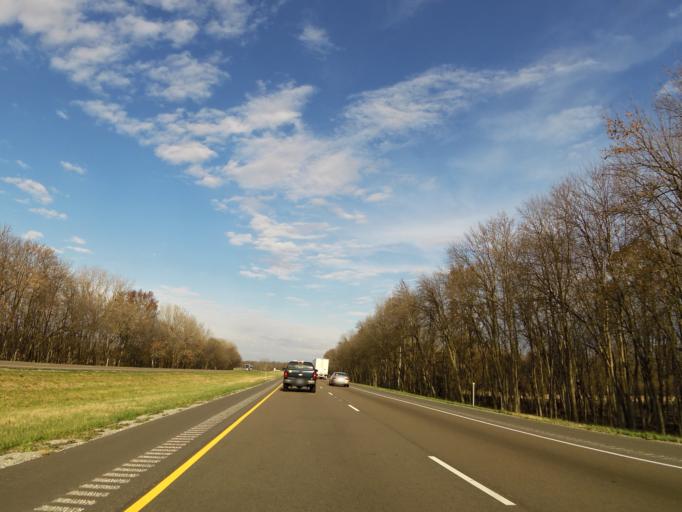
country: US
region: Illinois
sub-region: Washington County
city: Okawville
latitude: 38.4691
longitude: -89.5731
